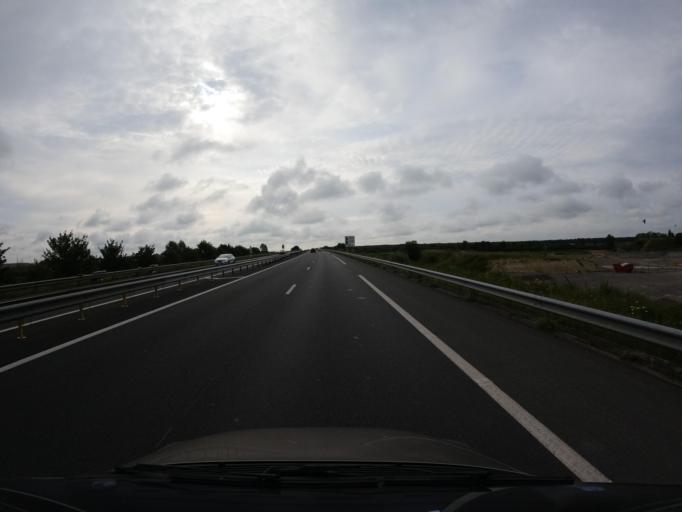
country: FR
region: Centre
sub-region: Departement d'Indre-et-Loire
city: Villandry
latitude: 47.3056
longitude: 0.5192
